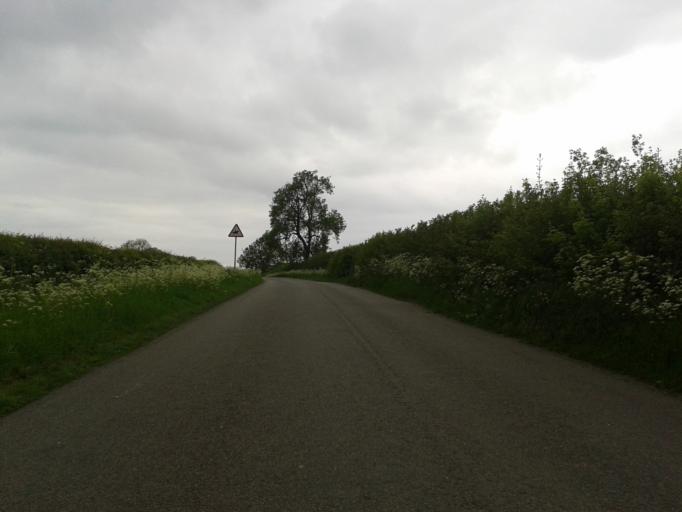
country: GB
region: England
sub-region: Leicestershire
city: Countesthorpe
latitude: 52.5236
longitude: -1.1483
